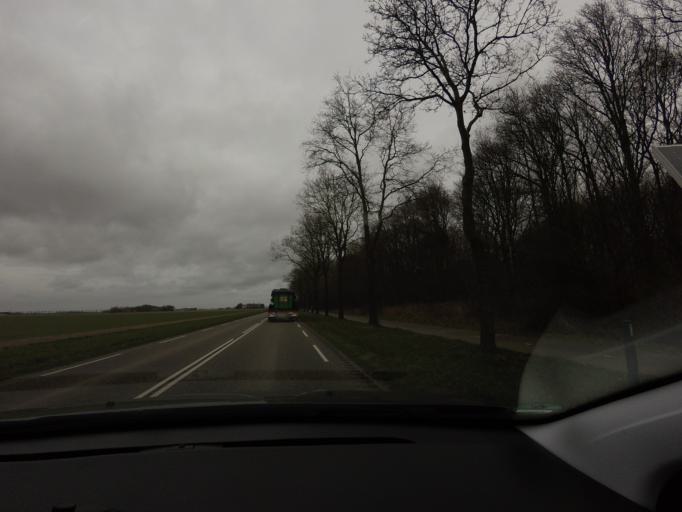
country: NL
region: Flevoland
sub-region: Gemeente Noordoostpolder
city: Emmeloord
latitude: 52.7137
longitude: 5.7198
